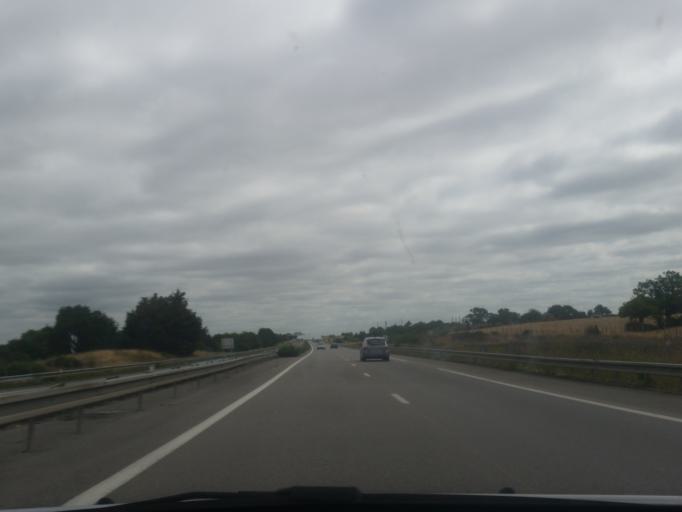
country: FR
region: Pays de la Loire
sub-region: Departement de la Loire-Atlantique
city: Ancenis
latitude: 47.4084
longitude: -1.1629
